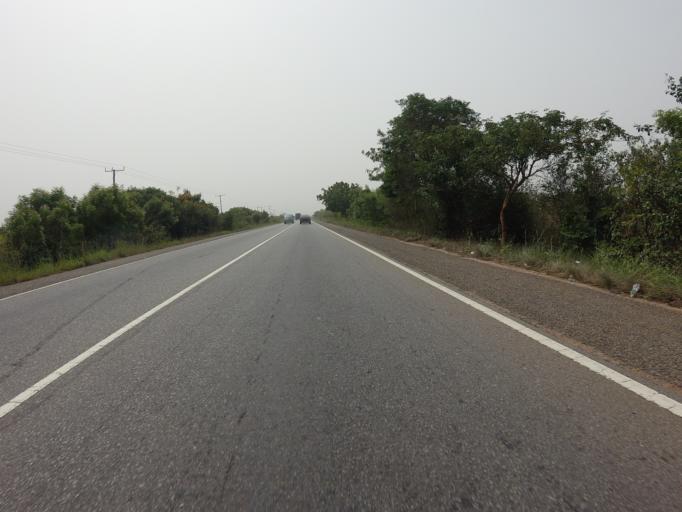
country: GH
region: Volta
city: Anloga
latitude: 5.9352
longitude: 0.5234
